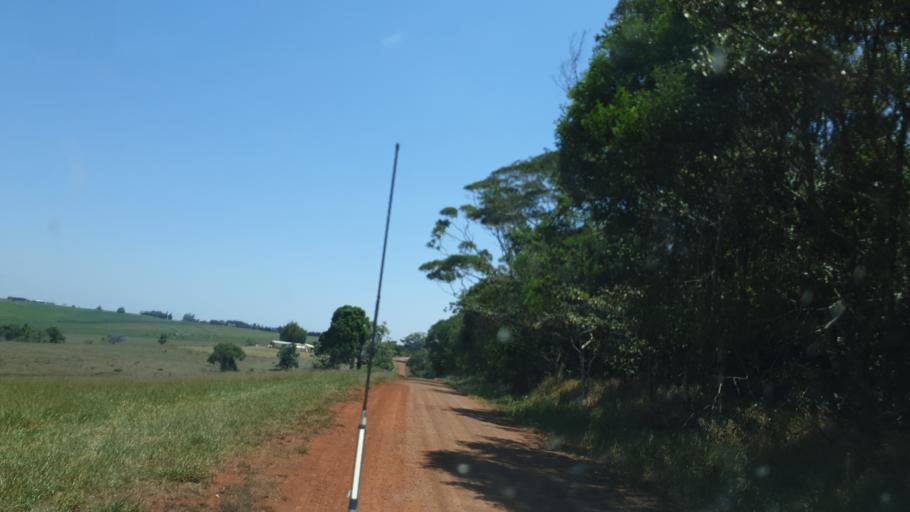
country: AU
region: Queensland
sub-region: Tablelands
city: Atherton
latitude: -17.3444
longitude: 145.6234
